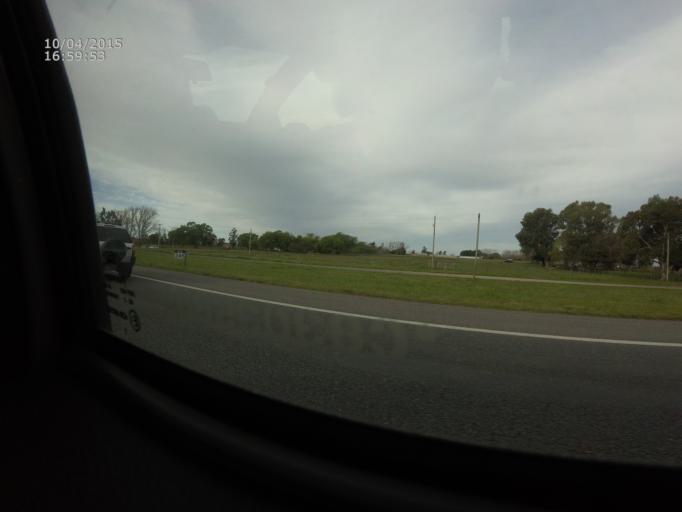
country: AR
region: Buenos Aires
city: Coronel Vidal
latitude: -37.4676
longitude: -57.7241
